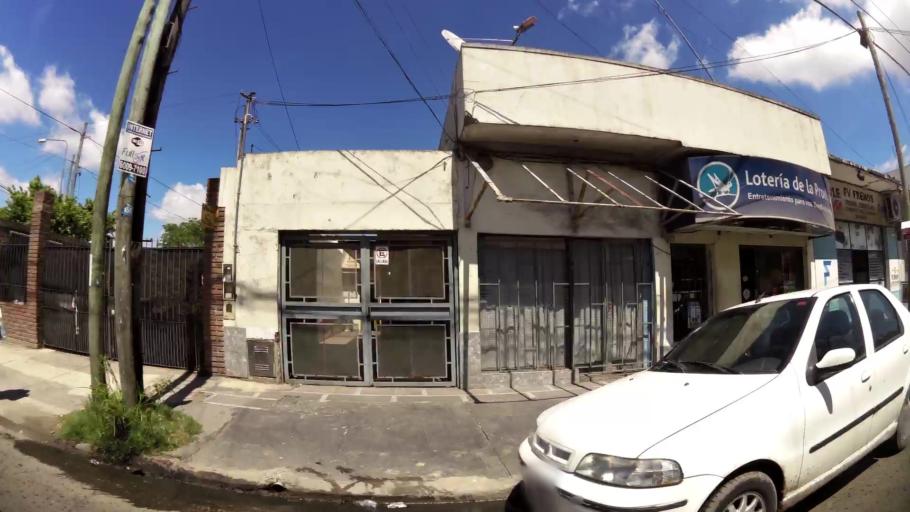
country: AR
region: Buenos Aires
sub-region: Partido de Lanus
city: Lanus
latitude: -34.6983
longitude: -58.4209
